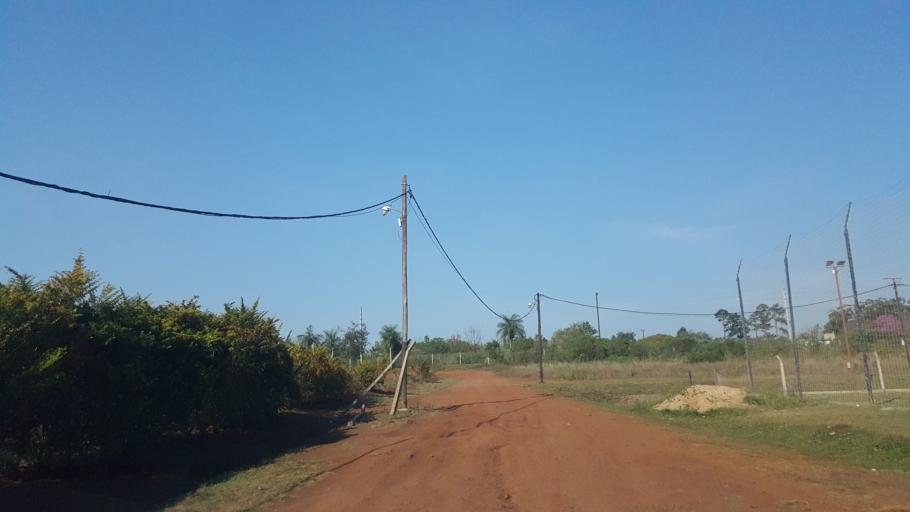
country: AR
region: Misiones
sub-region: Departamento de Capital
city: Posadas
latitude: -27.3951
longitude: -55.9773
